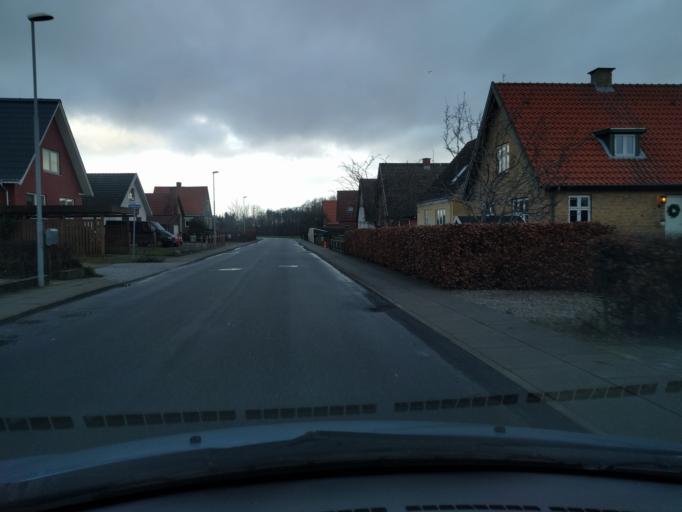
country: DK
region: South Denmark
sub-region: Kerteminde Kommune
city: Langeskov
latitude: 55.3645
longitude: 10.5866
